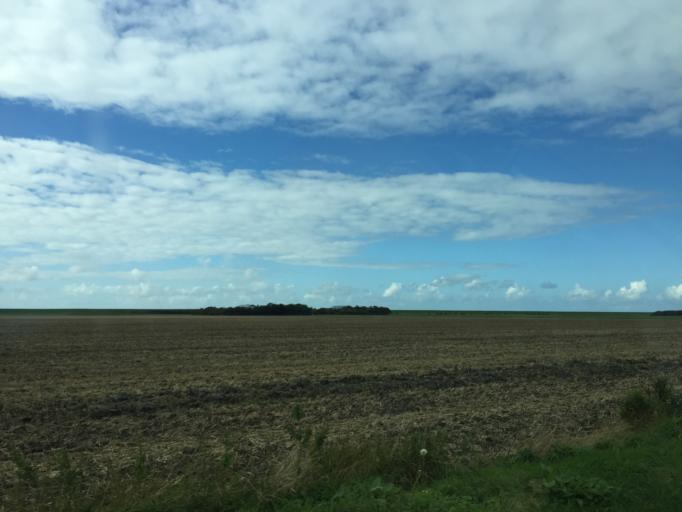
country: DE
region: Schleswig-Holstein
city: Friedrich-Wilhelm-Lubke-Koog
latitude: 54.8541
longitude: 8.6237
